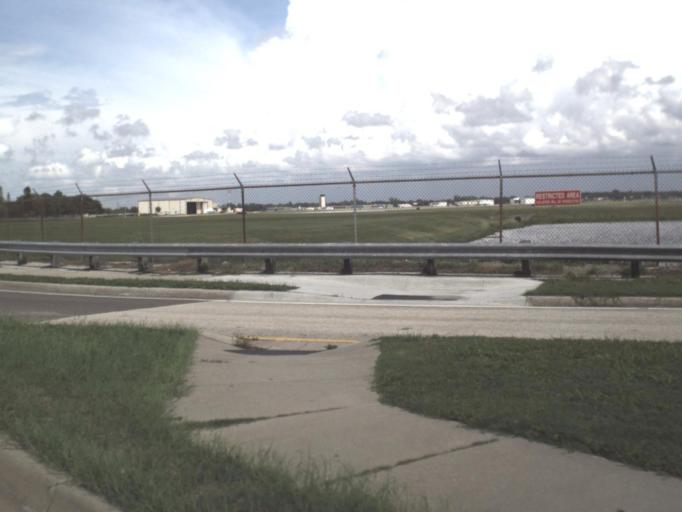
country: US
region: Florida
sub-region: Manatee County
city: Whitfield
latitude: 27.3871
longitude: -82.5585
